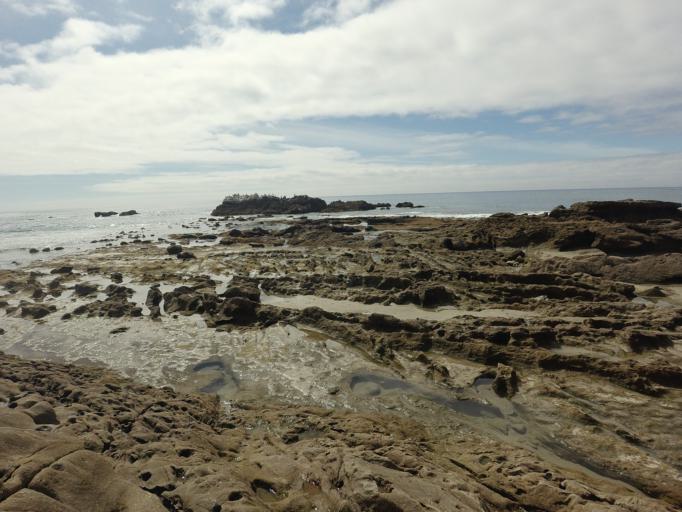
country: US
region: California
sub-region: Orange County
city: Laguna Beach
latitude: 33.5425
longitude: -117.7890
